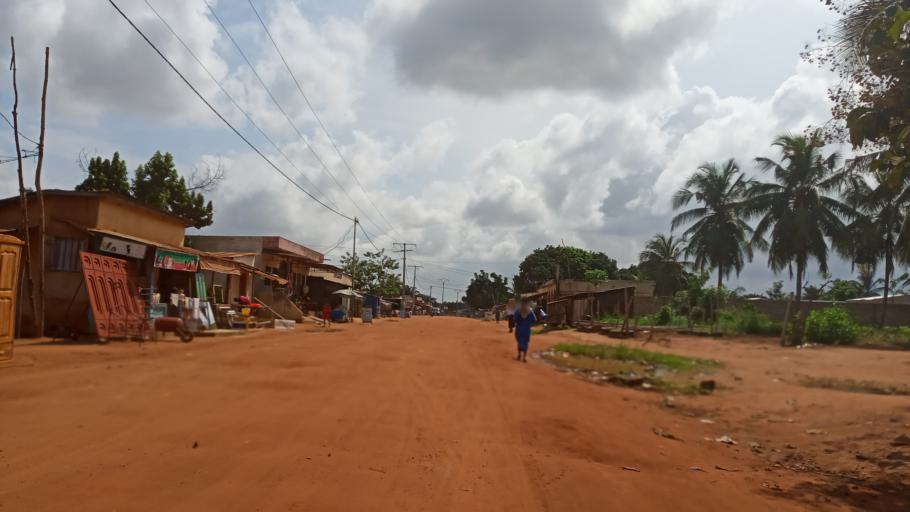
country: TG
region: Maritime
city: Lome
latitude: 6.2332
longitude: 1.1379
